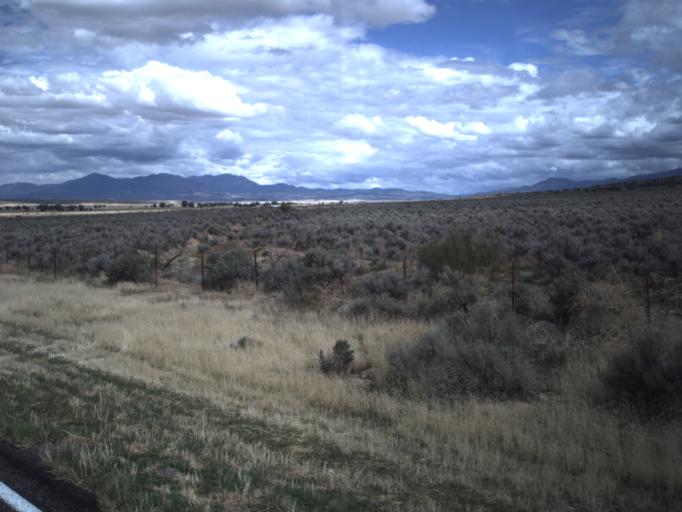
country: US
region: Utah
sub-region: Millard County
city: Fillmore
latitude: 39.0136
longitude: -112.4100
